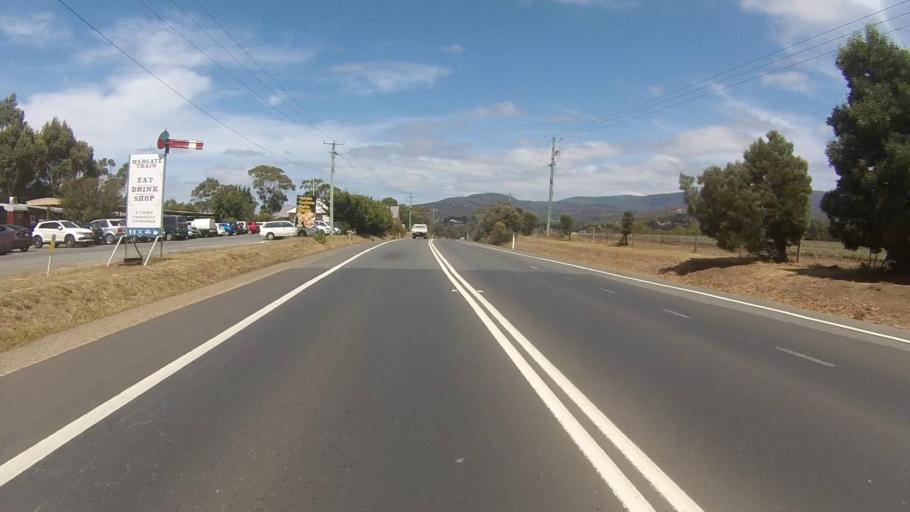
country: AU
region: Tasmania
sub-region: Kingborough
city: Margate
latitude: -43.0173
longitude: 147.2703
